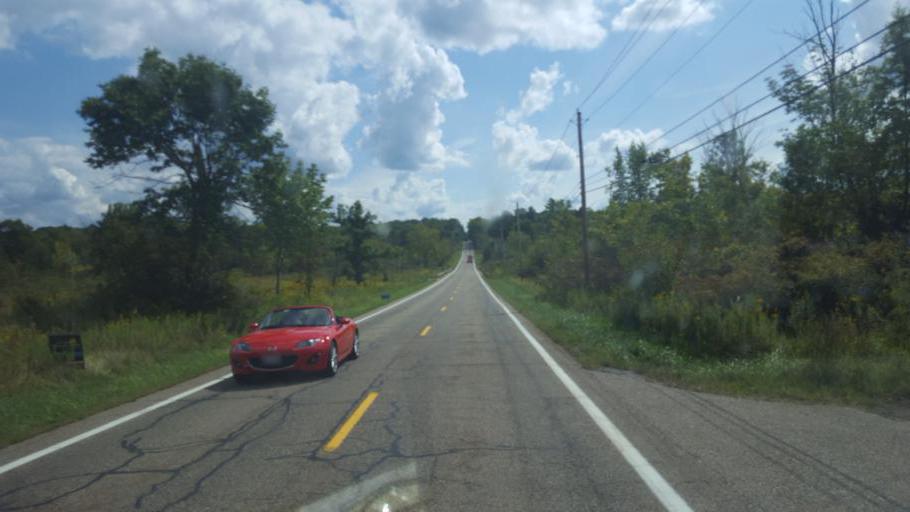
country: US
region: Ohio
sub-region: Portage County
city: Hiram
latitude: 41.2835
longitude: -81.1446
